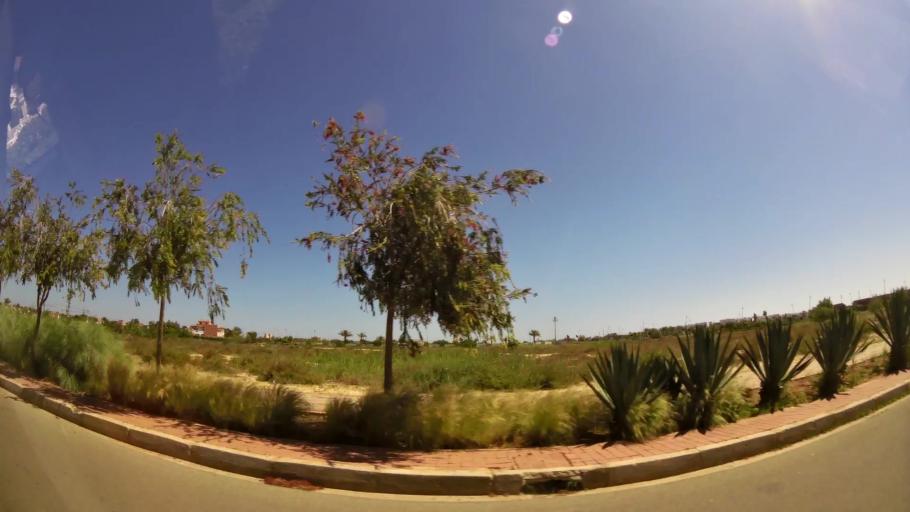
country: MA
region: Oriental
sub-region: Berkane-Taourirt
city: Madagh
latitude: 35.1004
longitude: -2.3012
